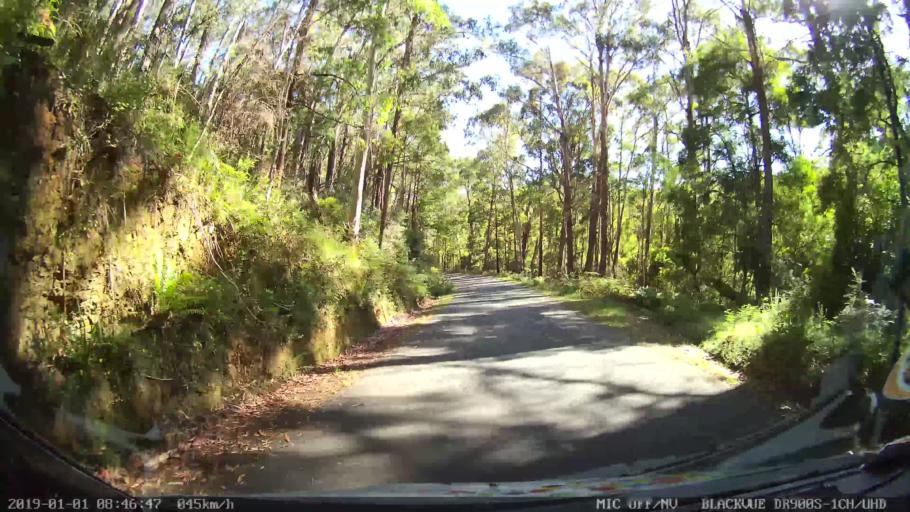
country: AU
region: New South Wales
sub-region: Snowy River
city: Jindabyne
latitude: -36.2981
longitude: 148.1946
